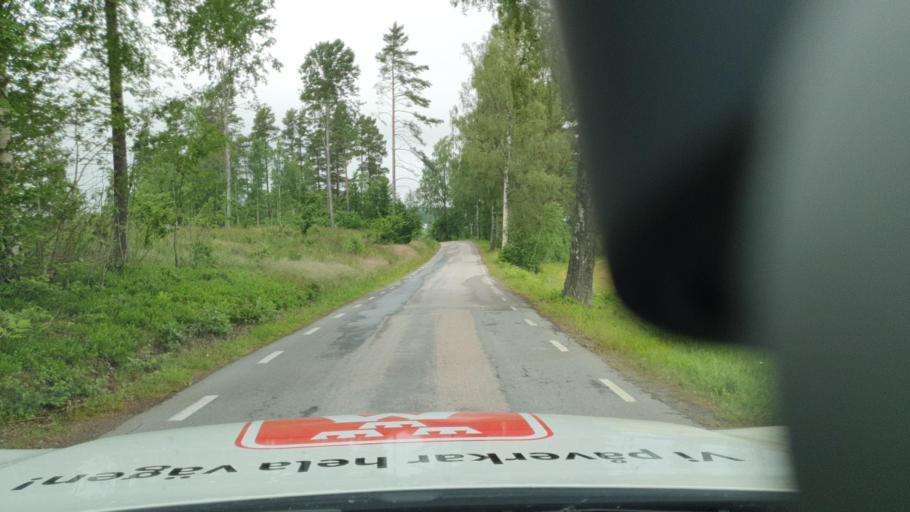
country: SE
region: Vaestra Goetaland
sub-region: Gullspangs Kommun
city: Gullspang
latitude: 59.0285
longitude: 14.1784
